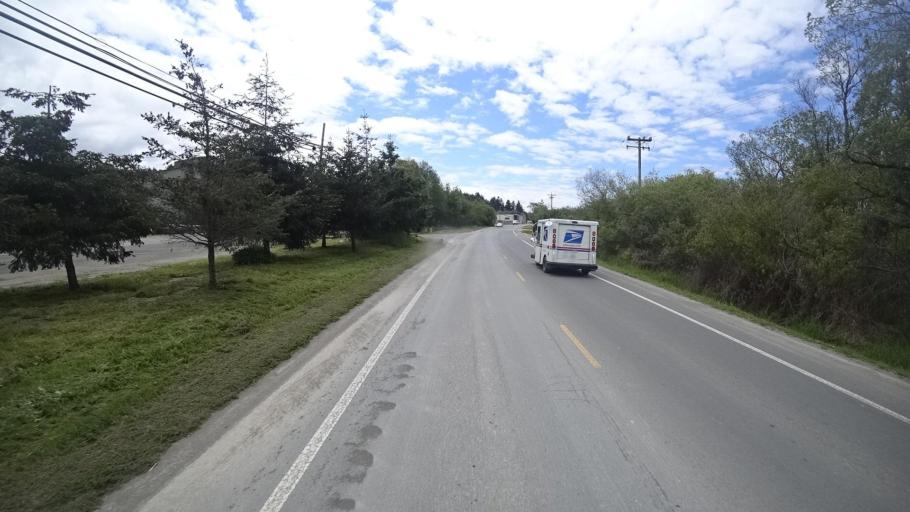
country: US
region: California
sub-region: Humboldt County
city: Arcata
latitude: 40.8985
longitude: -124.0749
